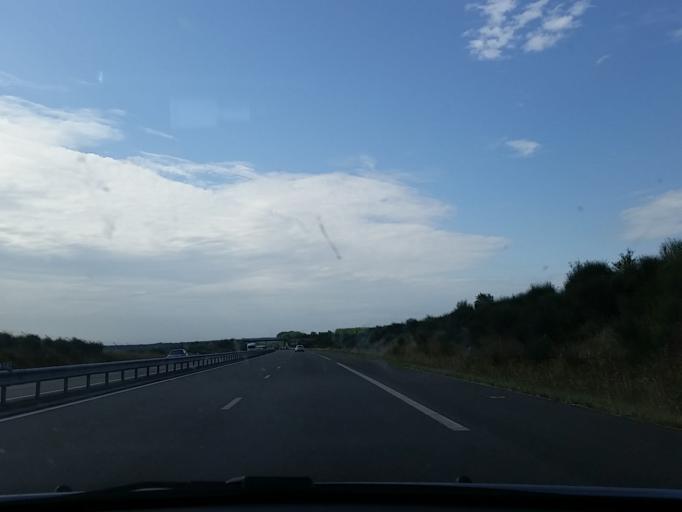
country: FR
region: Centre
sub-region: Departement du Cher
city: Levet
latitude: 46.8297
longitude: 2.4125
